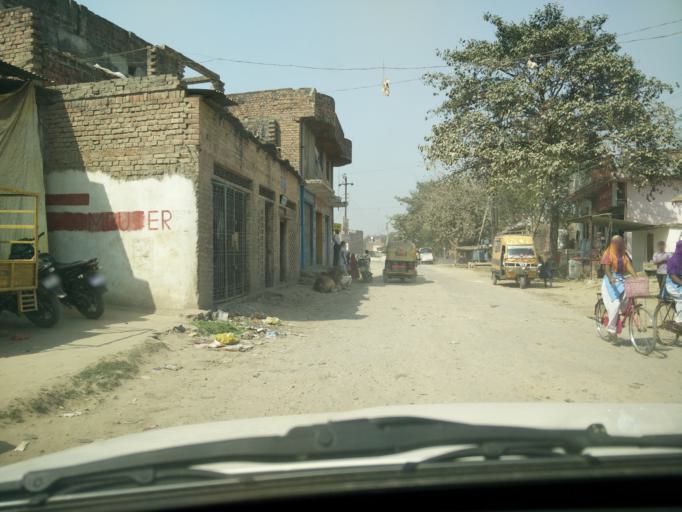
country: IN
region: Uttar Pradesh
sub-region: Varanasi
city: Ramnagar
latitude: 25.2627
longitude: 83.0187
